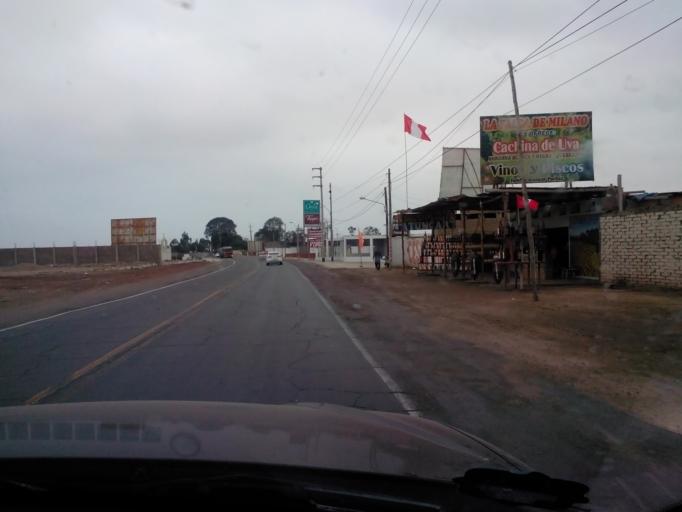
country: PE
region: Ica
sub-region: Provincia de Chincha
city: San Pedro
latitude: -13.4097
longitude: -76.1662
